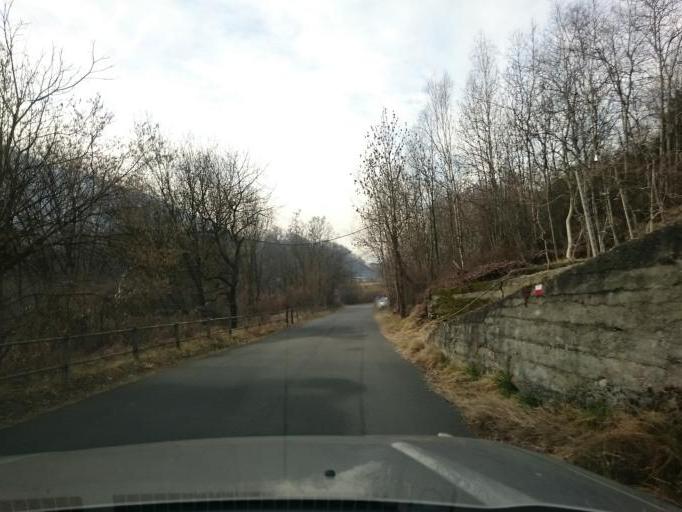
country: IT
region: Lombardy
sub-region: Provincia di Sondrio
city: Sernio
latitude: 46.2318
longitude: 10.2070
